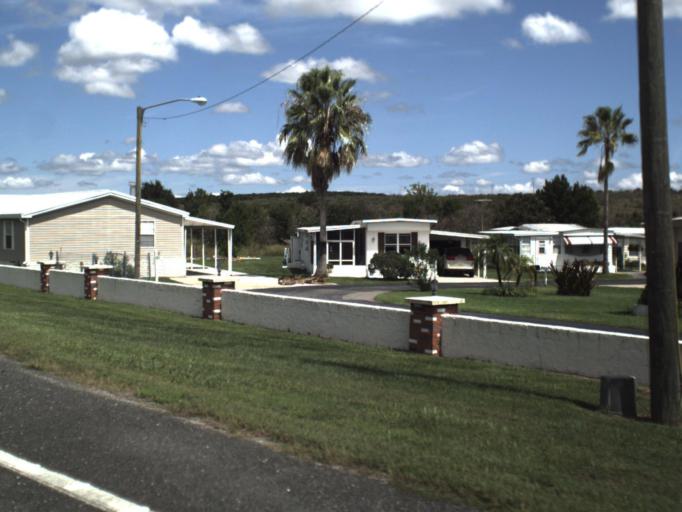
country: US
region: Florida
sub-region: Polk County
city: Dundee
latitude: 27.9894
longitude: -81.5949
